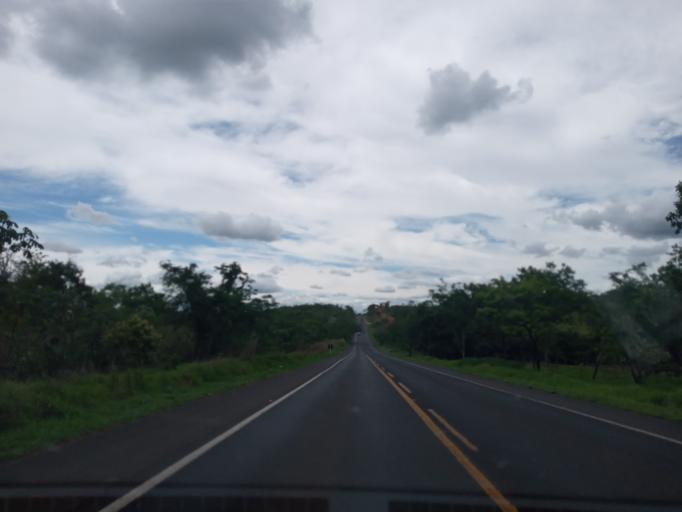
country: BR
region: Minas Gerais
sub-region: Uberlandia
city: Uberlandia
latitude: -19.1775
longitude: -47.8859
